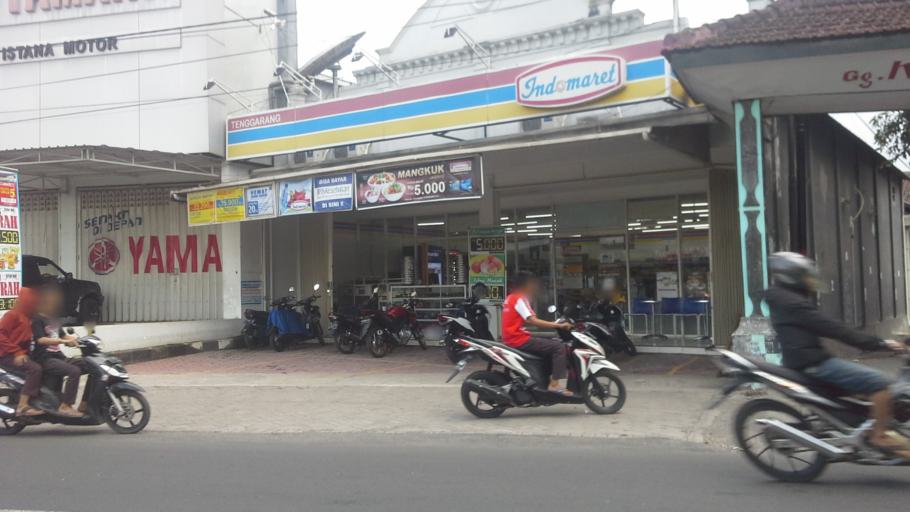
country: ID
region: East Java
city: Bondowoso
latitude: -7.9100
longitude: 113.8500
